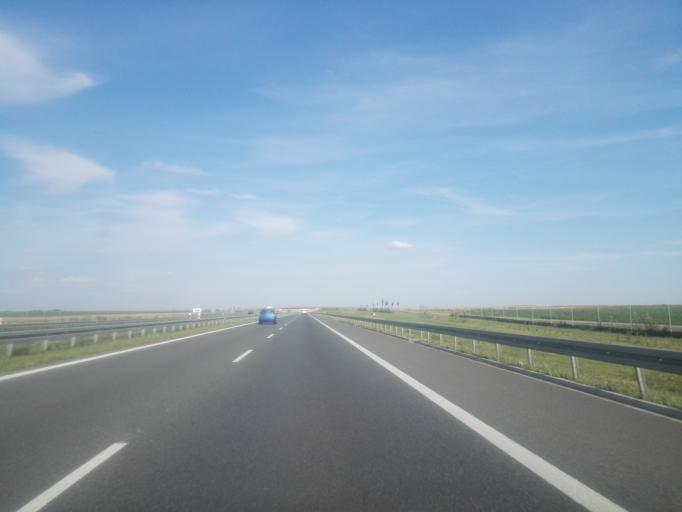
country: PL
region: Lower Silesian Voivodeship
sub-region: Powiat wroclawski
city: Dlugoleka
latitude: 51.2280
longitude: 17.2616
